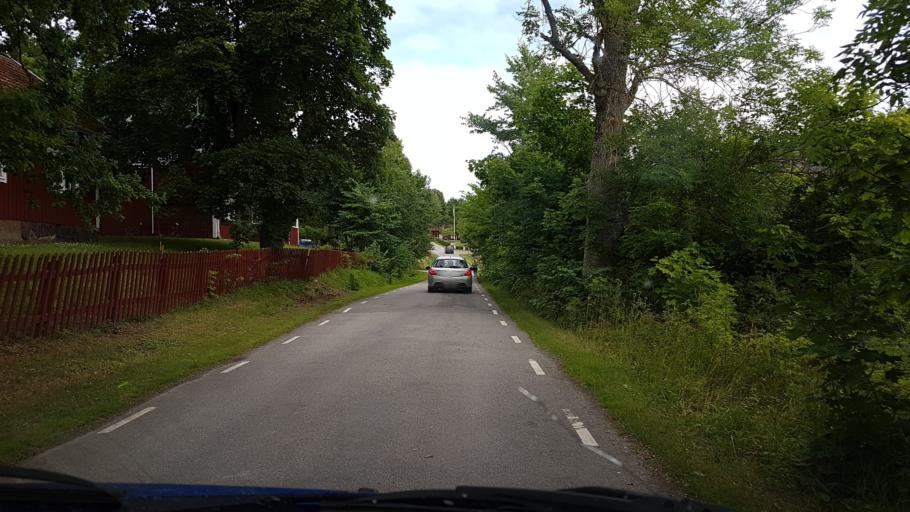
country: SE
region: OEstergoetland
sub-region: Valdemarsviks Kommun
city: Gusum
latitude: 58.4447
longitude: 16.5974
